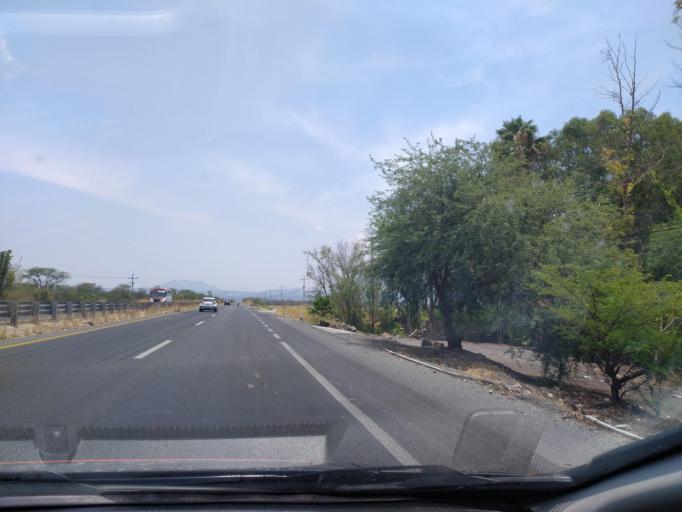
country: MX
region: Jalisco
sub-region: Acatlan de Juarez
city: Villa de los Ninos
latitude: 20.3704
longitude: -103.5924
